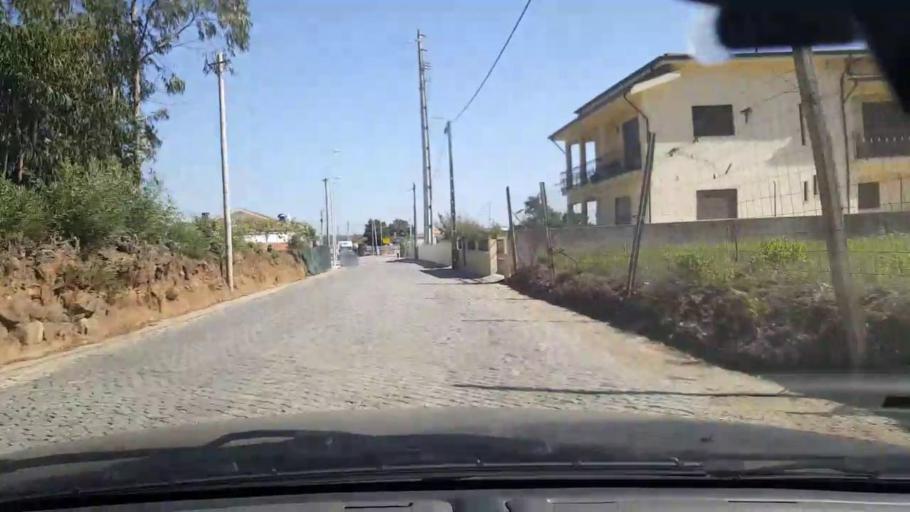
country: PT
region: Porto
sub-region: Matosinhos
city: Lavra
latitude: 41.2947
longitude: -8.7012
